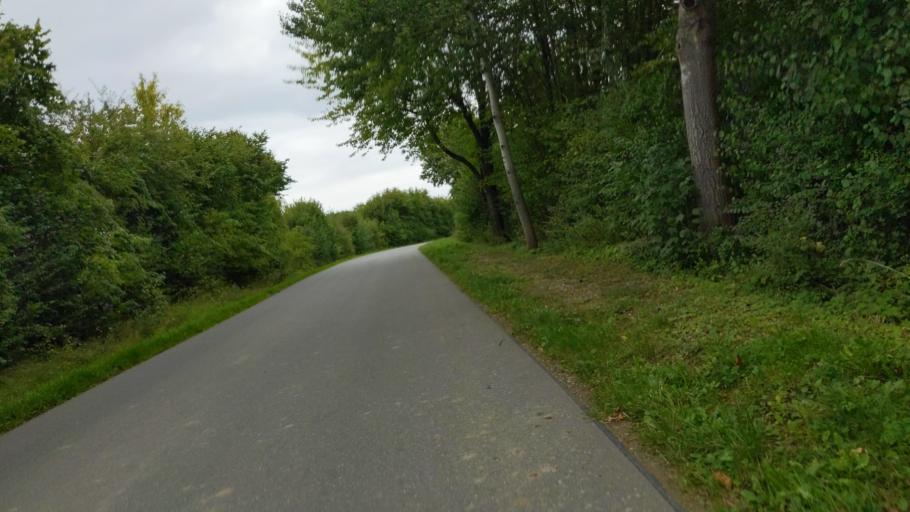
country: DE
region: Schleswig-Holstein
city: Buchholz
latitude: 53.7623
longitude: 10.7676
